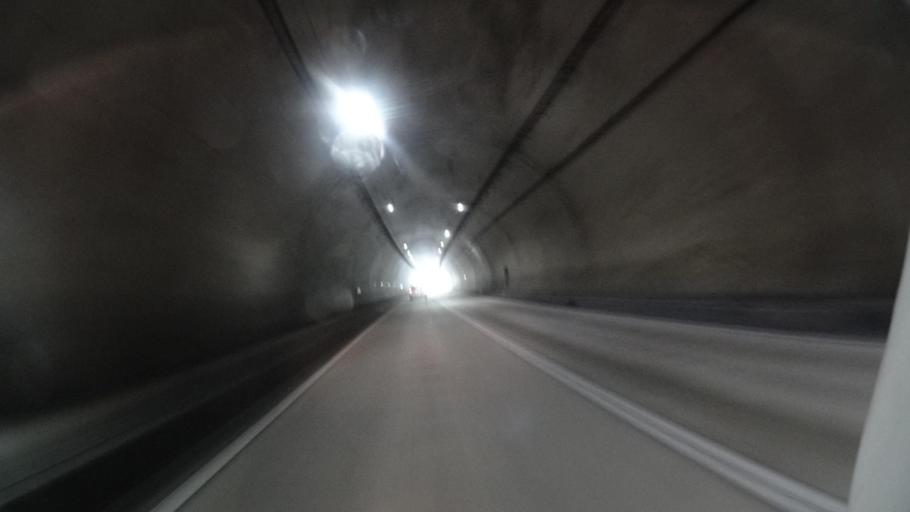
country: JP
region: Kyoto
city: Kameoka
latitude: 35.2228
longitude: 135.5721
